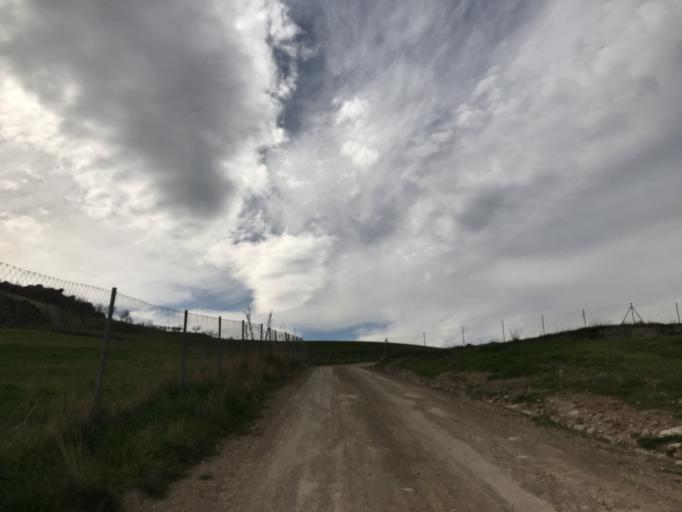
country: ES
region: Andalusia
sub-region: Provincia de Malaga
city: Ardales
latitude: 36.8743
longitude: -4.8792
